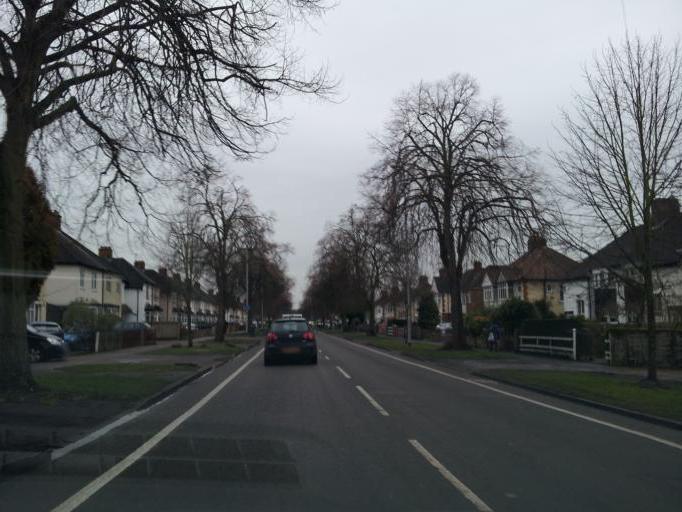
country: GB
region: England
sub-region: Cambridgeshire
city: Cambridge
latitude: 52.1851
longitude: 0.1518
